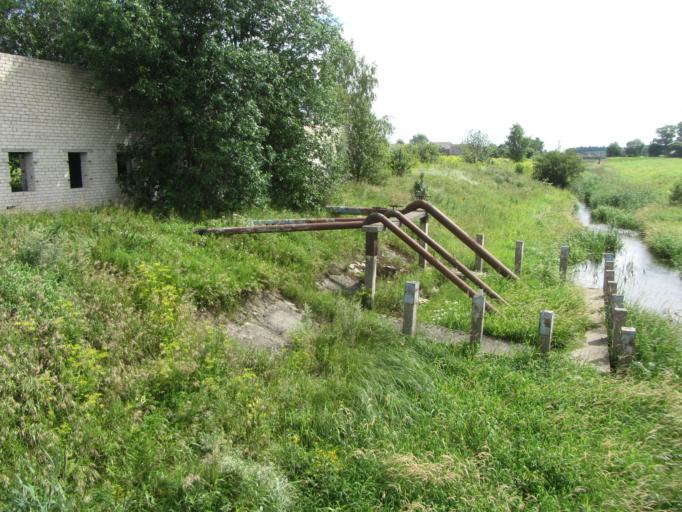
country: LT
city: Kalvarija
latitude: 54.3546
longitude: 23.3972
